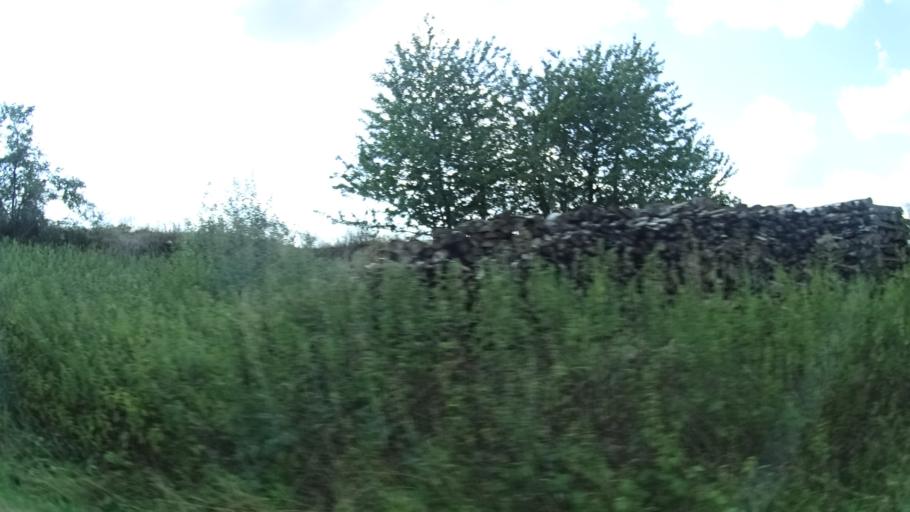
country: DE
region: Bavaria
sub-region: Regierungsbezirk Unterfranken
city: Trappstadt
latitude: 50.3115
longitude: 10.5707
